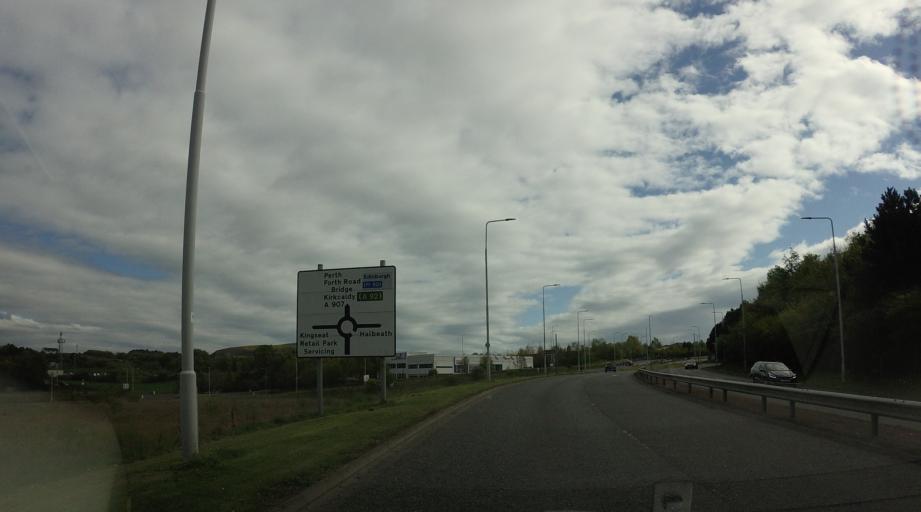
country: GB
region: Scotland
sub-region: Fife
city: Crossgates
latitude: 56.0815
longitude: -3.4050
